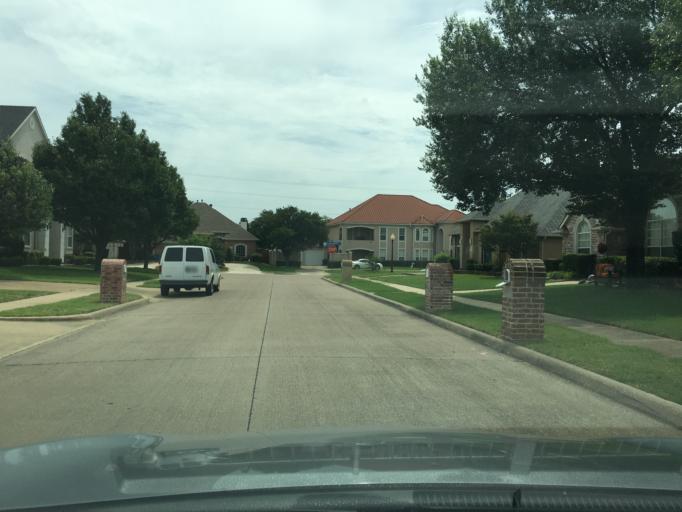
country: US
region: Texas
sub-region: Dallas County
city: Richardson
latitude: 32.9335
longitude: -96.7150
